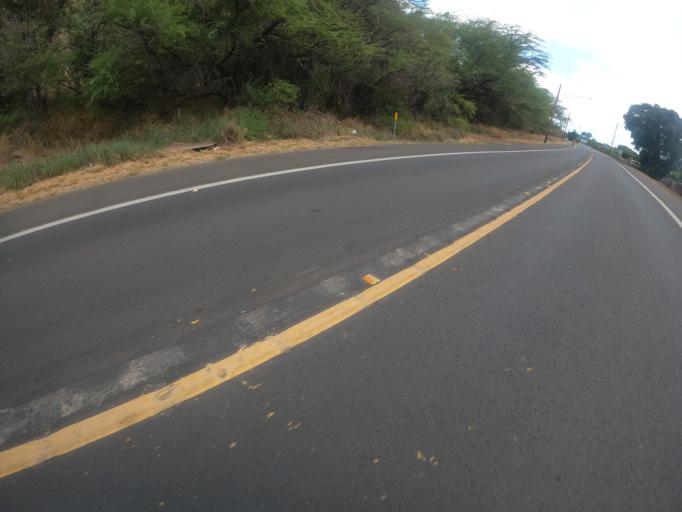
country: US
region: Hawaii
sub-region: Honolulu County
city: Makaha
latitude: 21.4836
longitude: -158.2288
